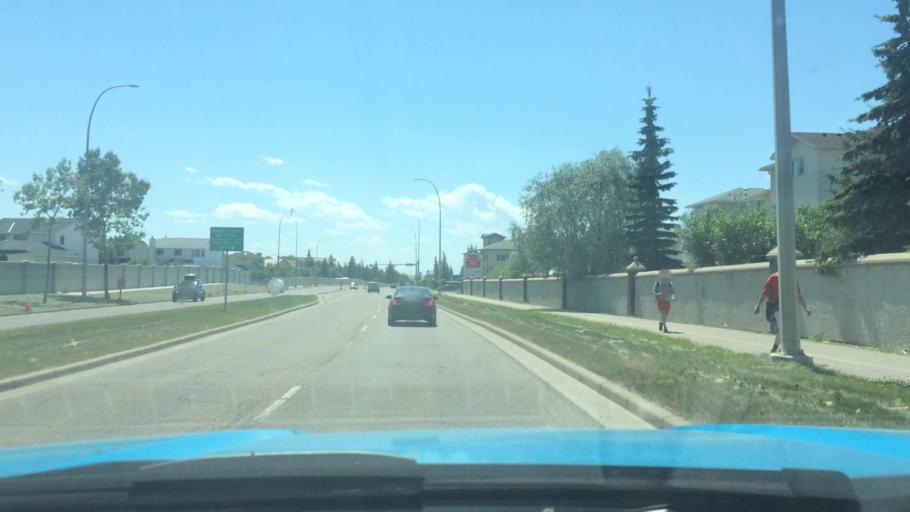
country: CA
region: Alberta
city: Calgary
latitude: 51.1391
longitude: -114.1841
